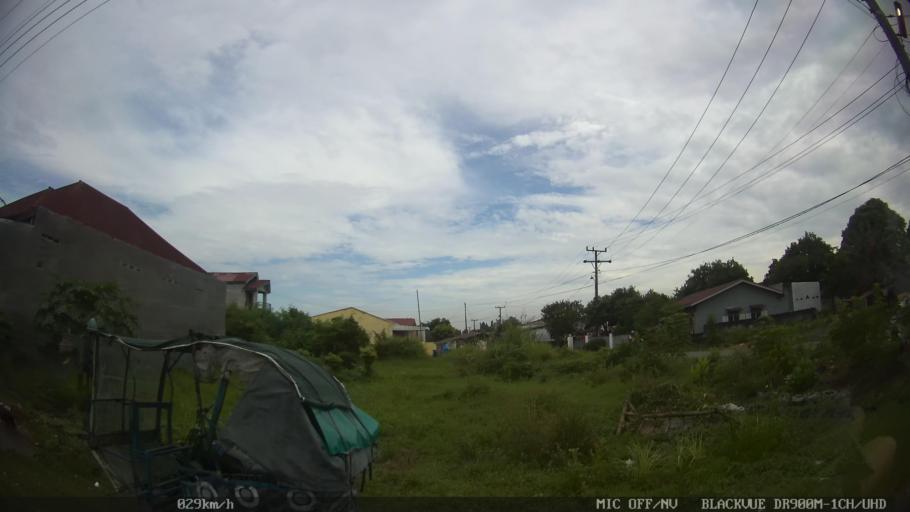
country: ID
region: North Sumatra
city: Sunggal
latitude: 3.6140
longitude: 98.5997
